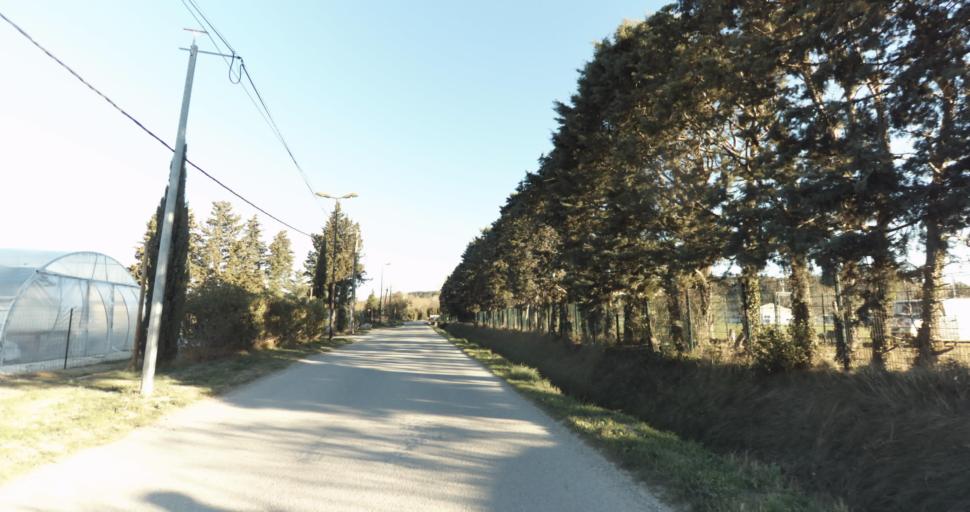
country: FR
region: Provence-Alpes-Cote d'Azur
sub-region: Departement des Bouches-du-Rhone
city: Barbentane
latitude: 43.9032
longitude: 4.7411
